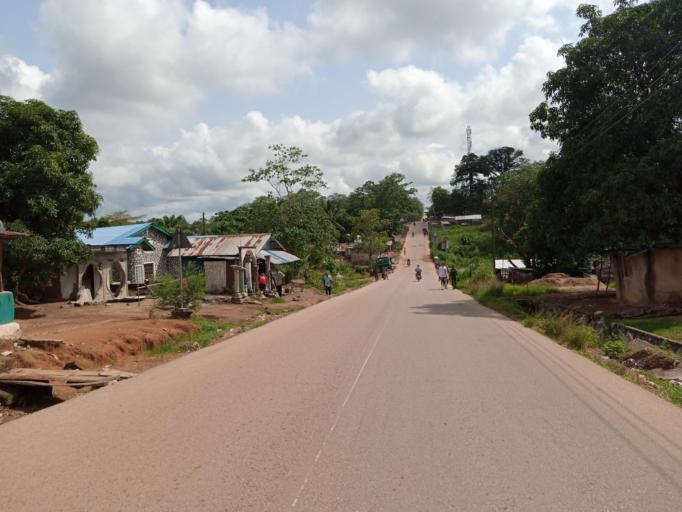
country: SL
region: Southern Province
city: Bo
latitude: 7.9786
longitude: -11.7388
